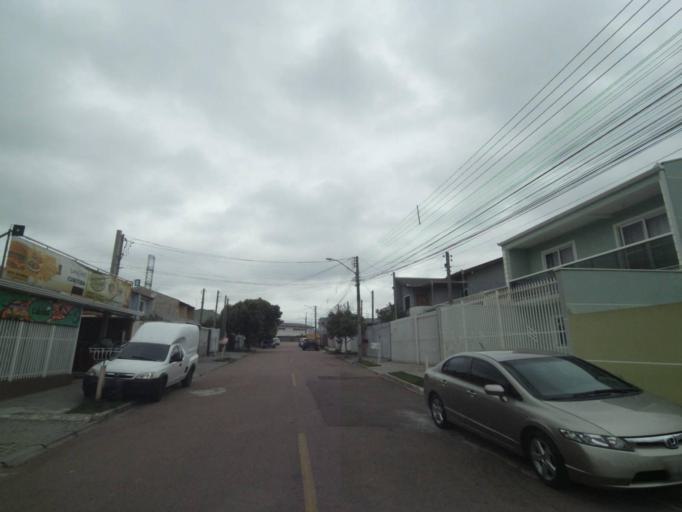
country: BR
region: Parana
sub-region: Araucaria
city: Araucaria
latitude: -25.5414
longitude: -49.3383
